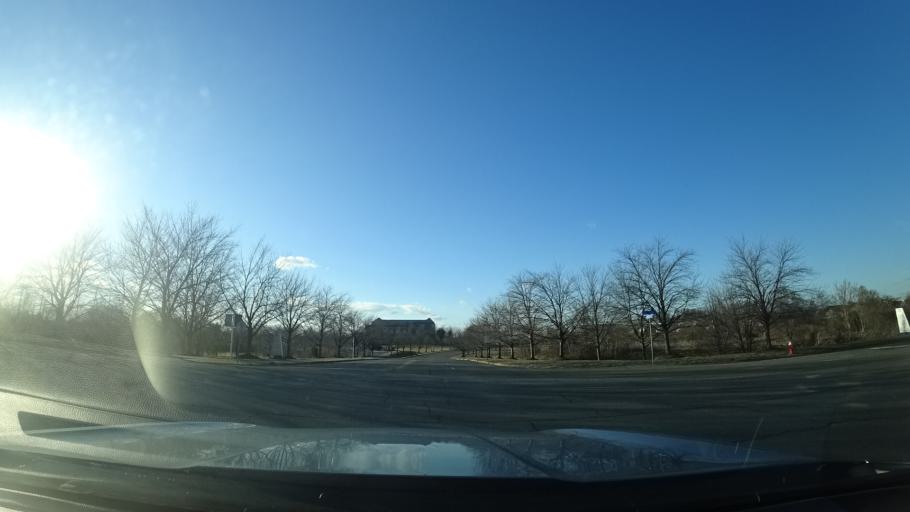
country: US
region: Virginia
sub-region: Loudoun County
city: University Center
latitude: 39.0534
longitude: -77.4408
